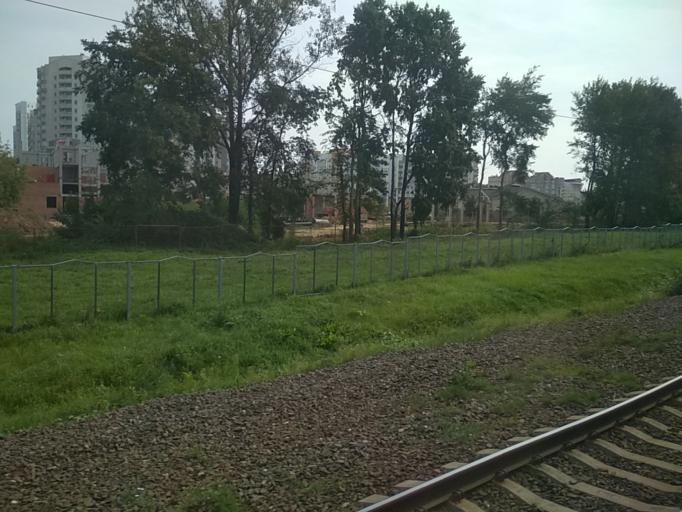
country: BY
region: Minsk
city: Syenitsa
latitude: 53.8455
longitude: 27.5560
